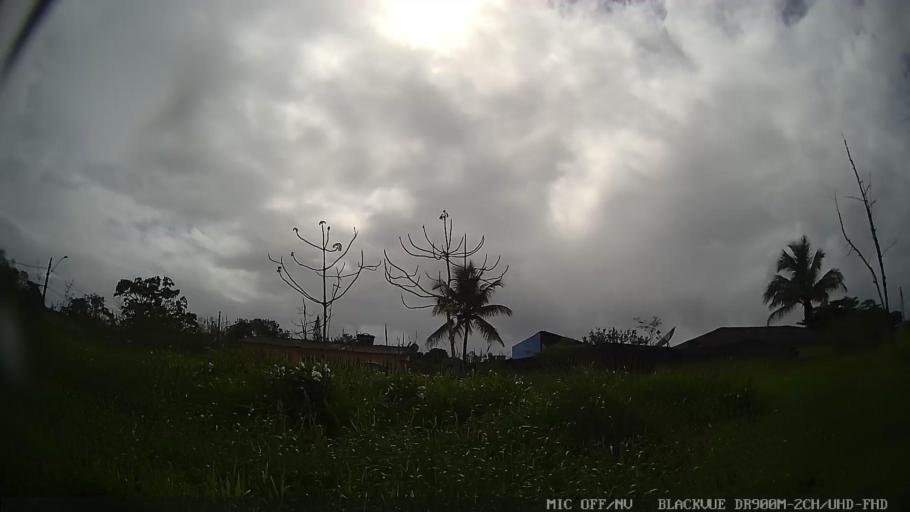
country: BR
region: Sao Paulo
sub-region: Itanhaem
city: Itanhaem
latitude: -24.2259
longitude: -46.9022
